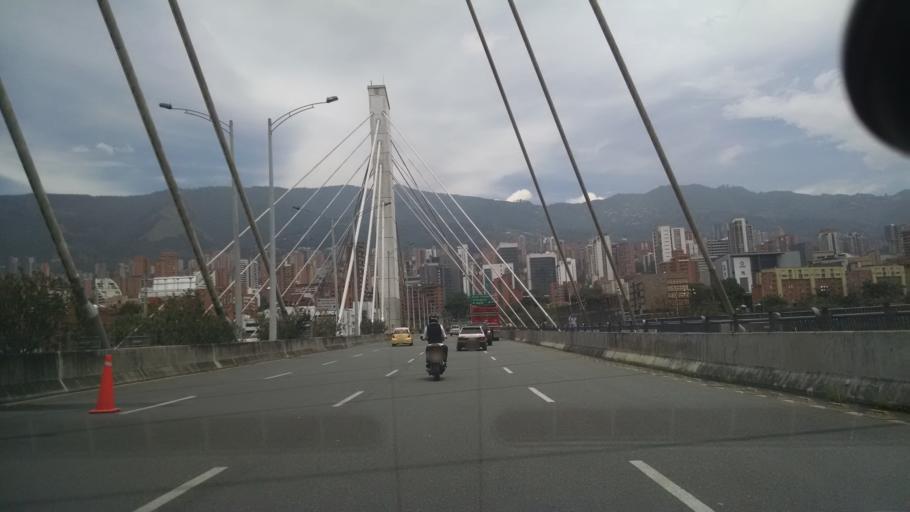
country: CO
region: Antioquia
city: Itagui
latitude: 6.2040
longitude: -75.5797
